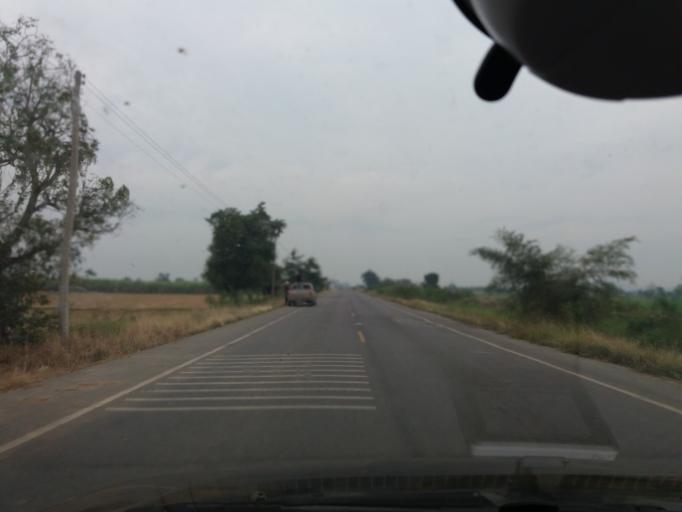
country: TH
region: Suphan Buri
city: Doem Bang Nang Buat
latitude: 14.8903
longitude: 100.1316
